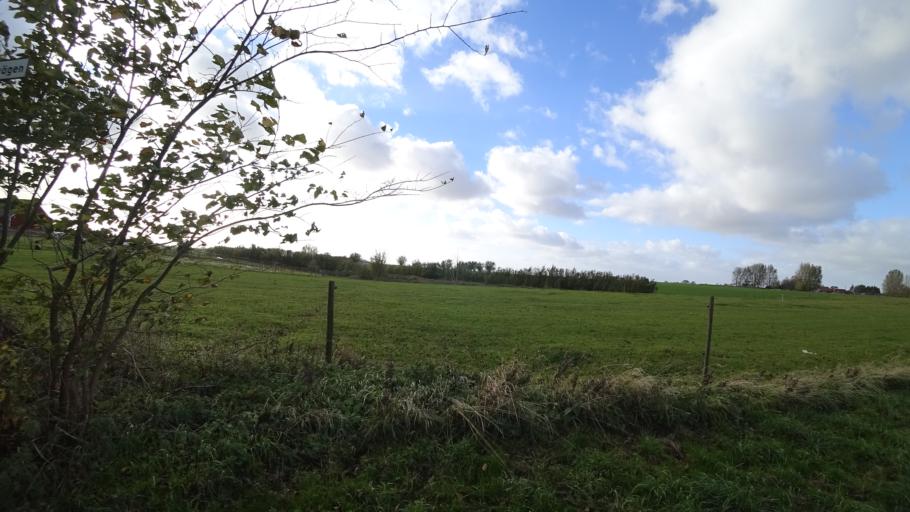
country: SE
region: Skane
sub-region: Staffanstorps Kommun
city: Staffanstorp
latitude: 55.6172
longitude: 13.2049
